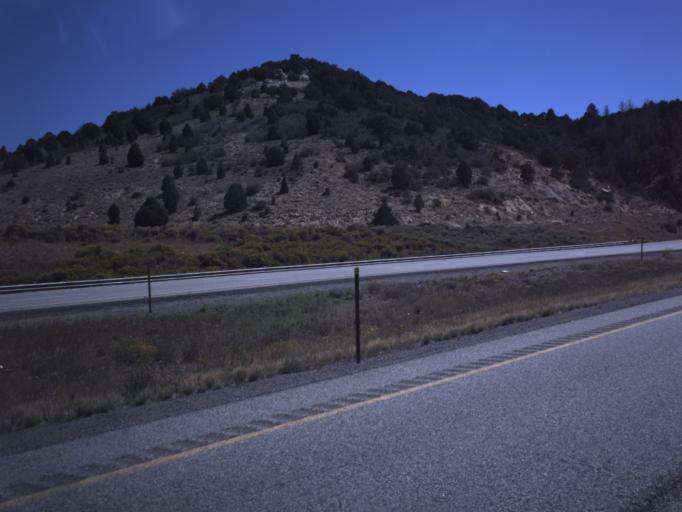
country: US
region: Utah
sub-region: Sevier County
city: Salina
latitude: 38.7961
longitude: -111.5097
